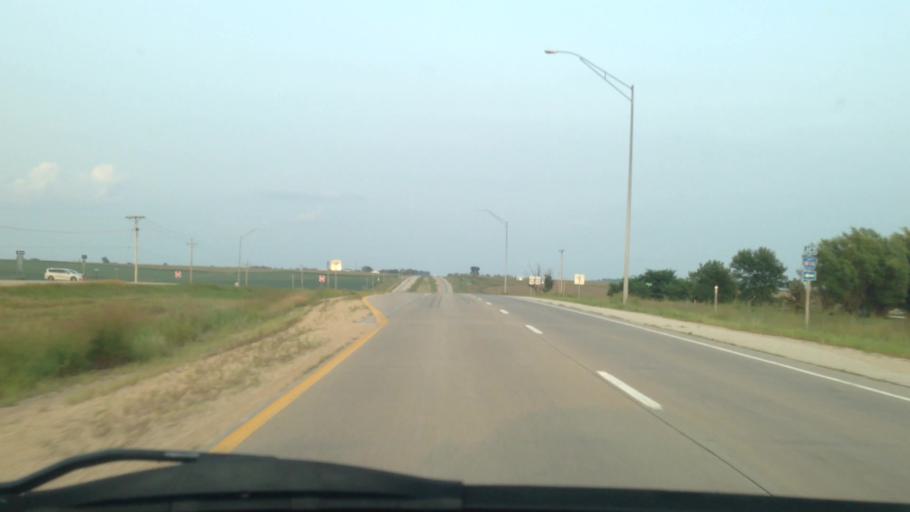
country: US
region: Iowa
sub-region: Benton County
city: Atkins
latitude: 41.9632
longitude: -91.9718
